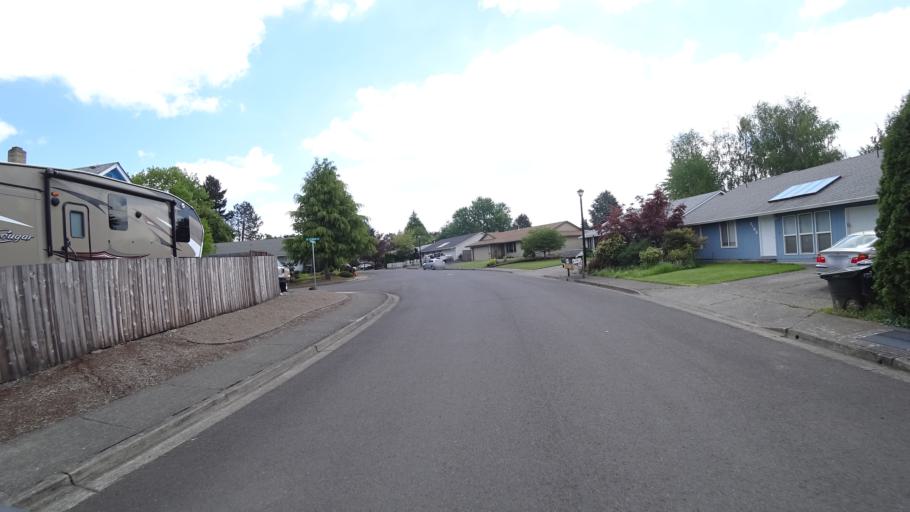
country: US
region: Oregon
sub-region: Washington County
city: Aloha
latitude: 45.5039
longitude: -122.8893
